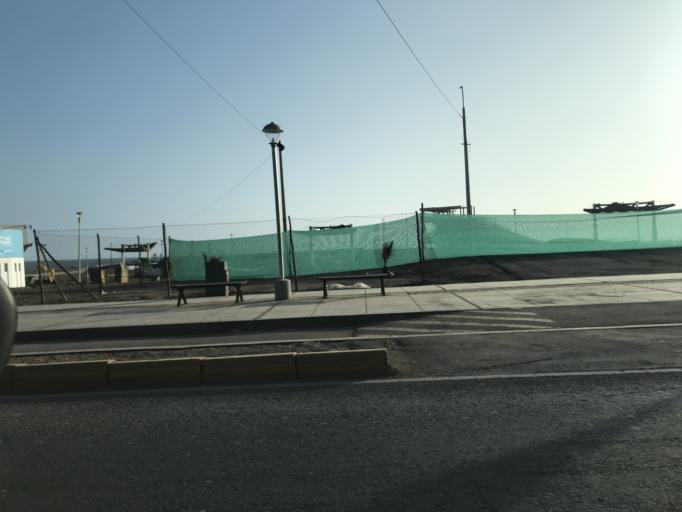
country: PE
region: Lima
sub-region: Lima
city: San Isidro
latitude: -12.0933
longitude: -77.0817
